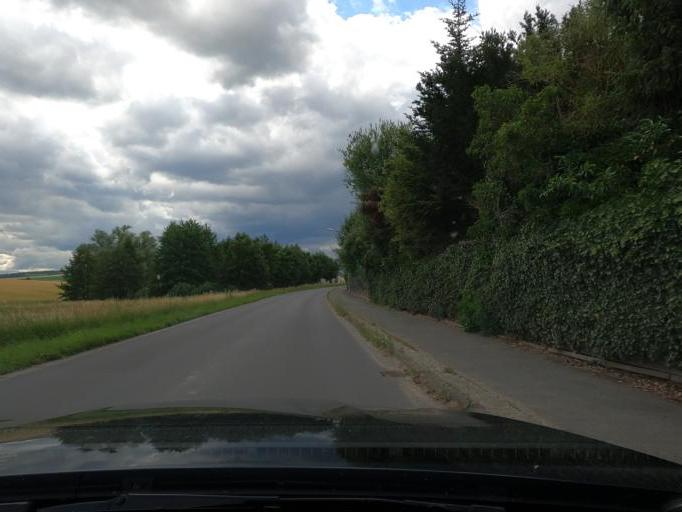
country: DE
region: Lower Saxony
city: Baddeckenstedt
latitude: 52.0967
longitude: 10.2297
